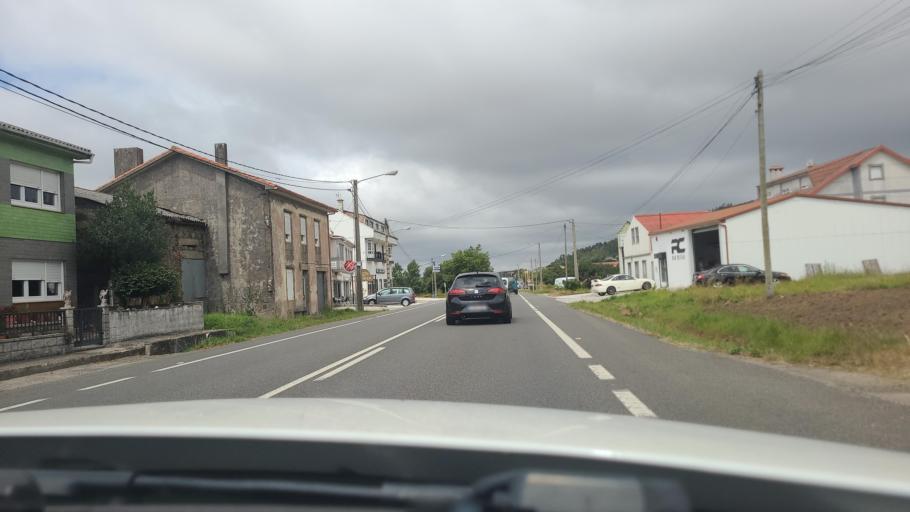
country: ES
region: Galicia
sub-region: Provincia da Coruna
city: Cee
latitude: 42.9825
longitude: -9.1865
